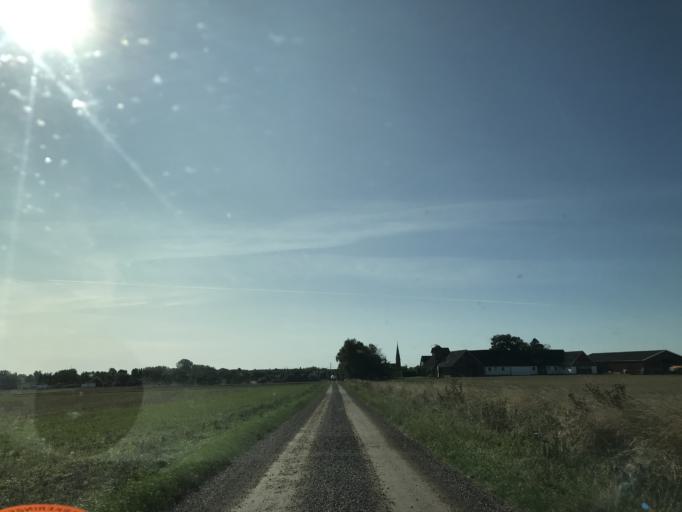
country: SE
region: Skane
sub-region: Landskrona
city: Asmundtorp
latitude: 55.8959
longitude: 12.9489
